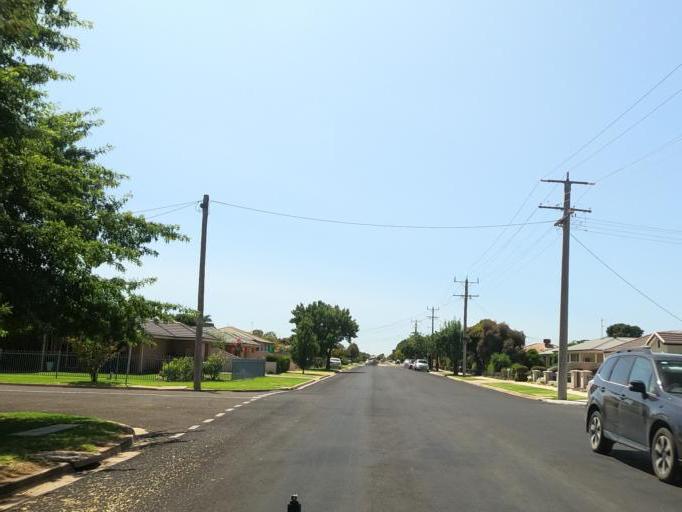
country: AU
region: Victoria
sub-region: Moira
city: Yarrawonga
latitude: -36.0091
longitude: 146.0110
